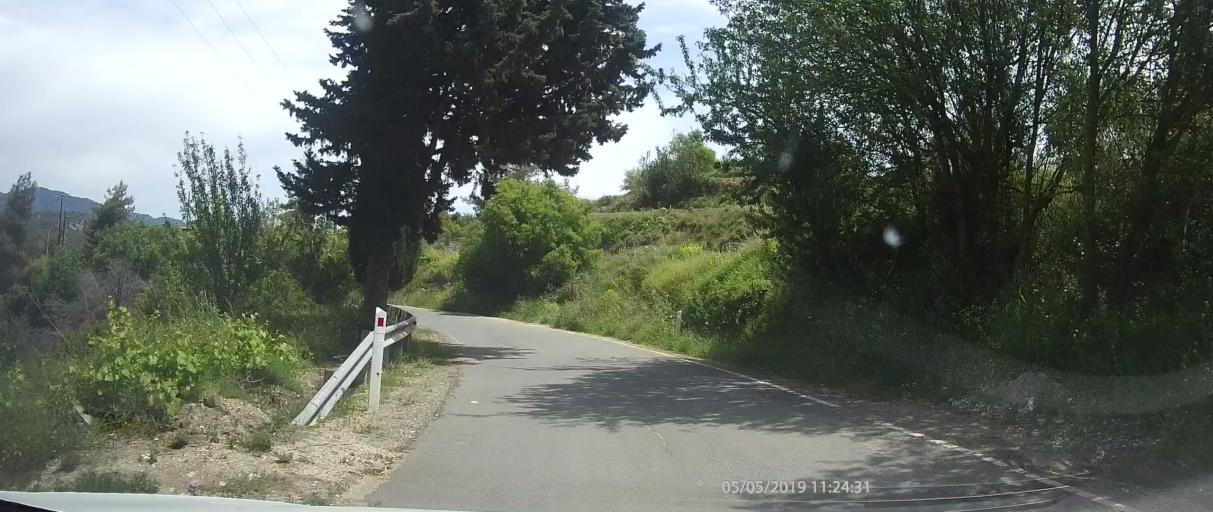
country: CY
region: Limassol
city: Pachna
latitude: 34.9213
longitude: 32.6402
